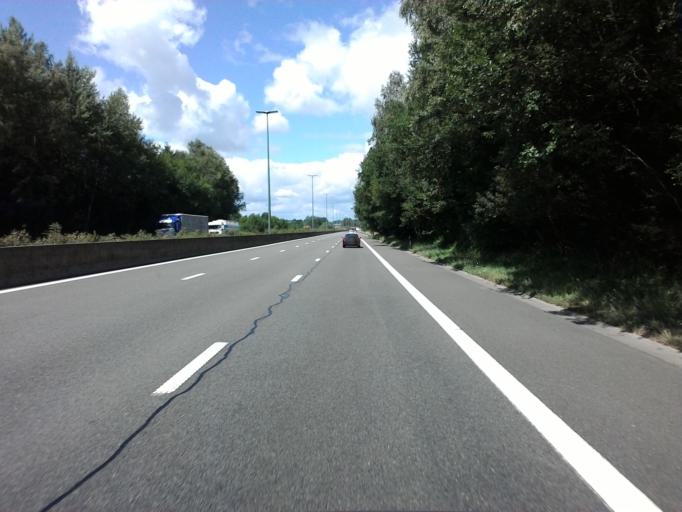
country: BE
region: Wallonia
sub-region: Province du Luxembourg
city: Habay-la-Vieille
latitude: 49.6995
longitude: 5.6499
